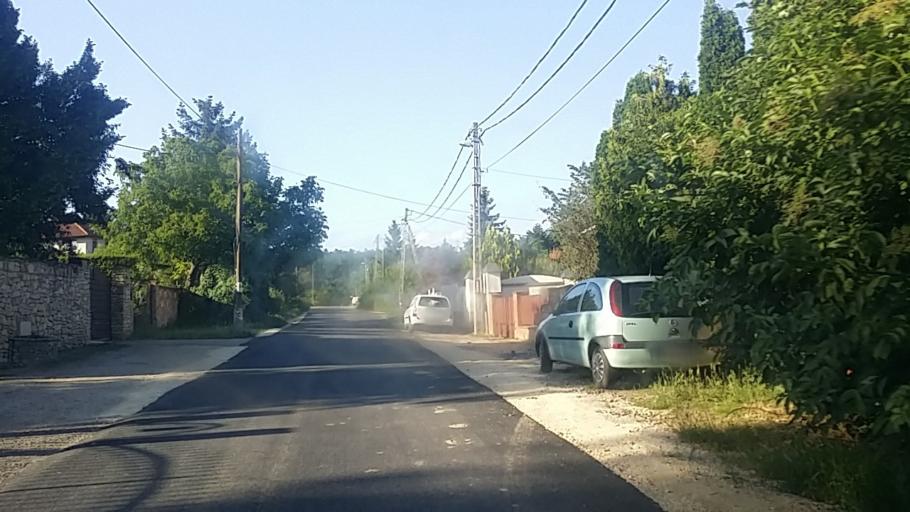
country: HU
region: Pest
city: Urom
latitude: 47.5812
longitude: 19.0186
